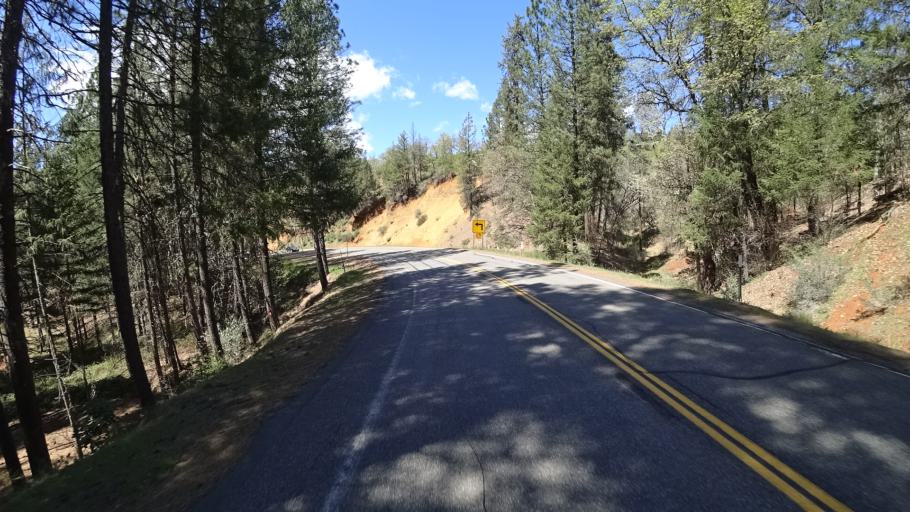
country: US
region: California
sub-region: Trinity County
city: Weaverville
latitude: 40.7552
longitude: -122.9084
